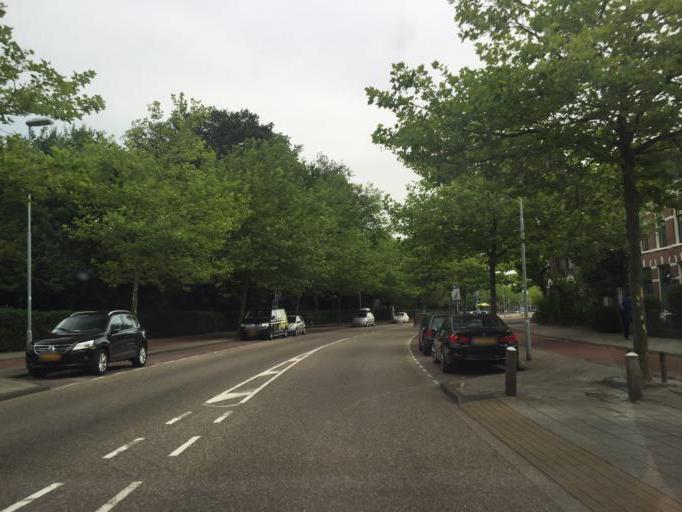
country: NL
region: North Holland
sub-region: Gemeente Haarlem
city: Haarlem
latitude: 52.3963
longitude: 4.6416
